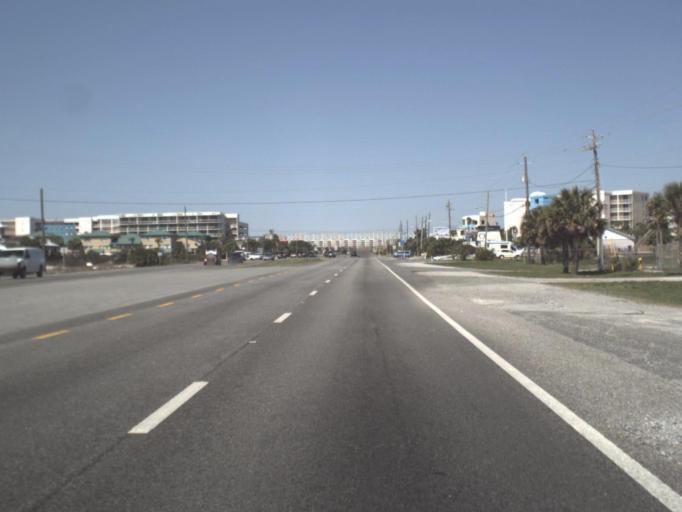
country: US
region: Florida
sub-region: Okaloosa County
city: Fort Walton Beach
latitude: 30.3956
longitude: -86.5827
